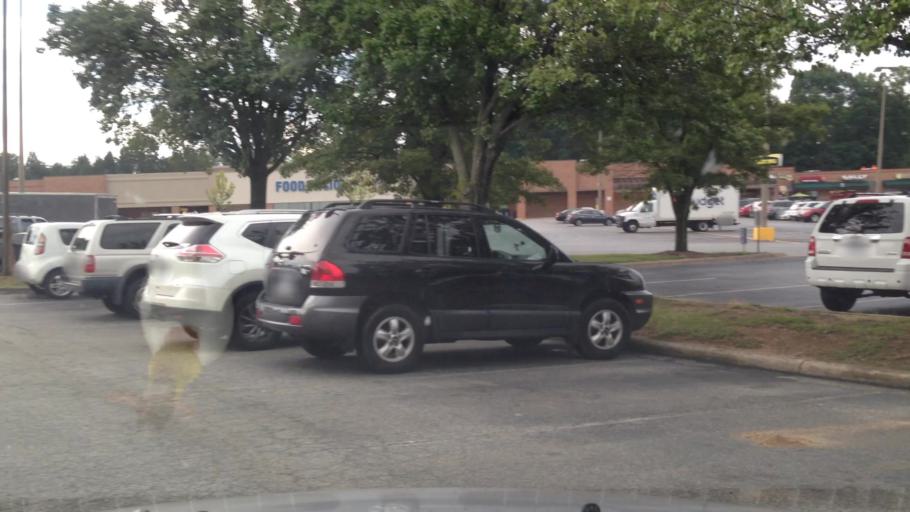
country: US
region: North Carolina
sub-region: Forsyth County
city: Kernersville
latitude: 36.1088
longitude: -80.0967
